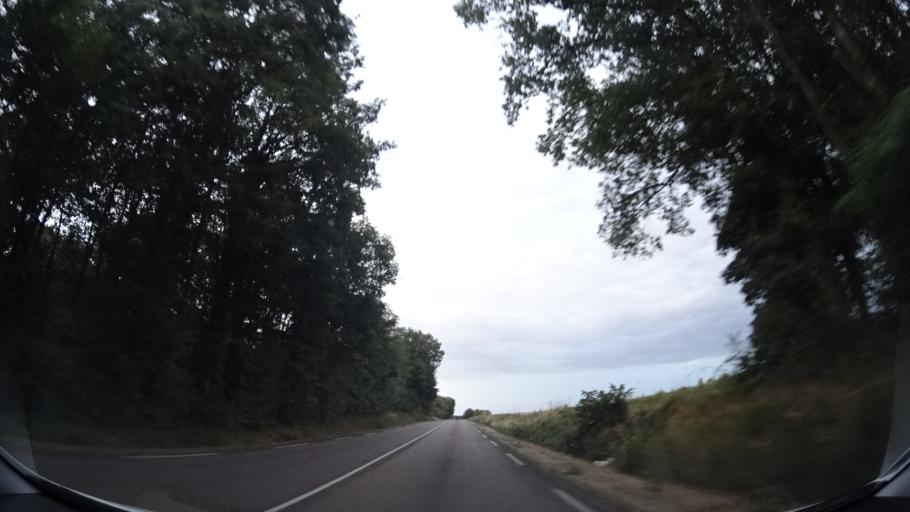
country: FR
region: Bourgogne
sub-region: Departement de l'Yonne
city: Cezy
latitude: 47.9378
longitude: 3.2609
